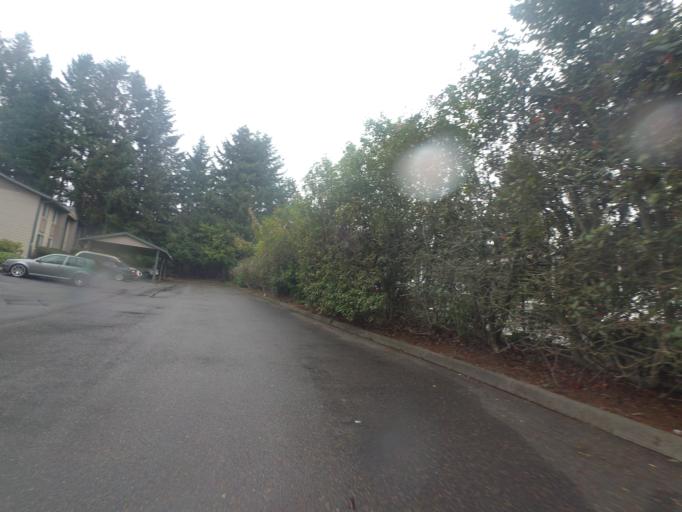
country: US
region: Washington
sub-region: Pierce County
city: University Place
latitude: 47.2194
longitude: -122.5397
